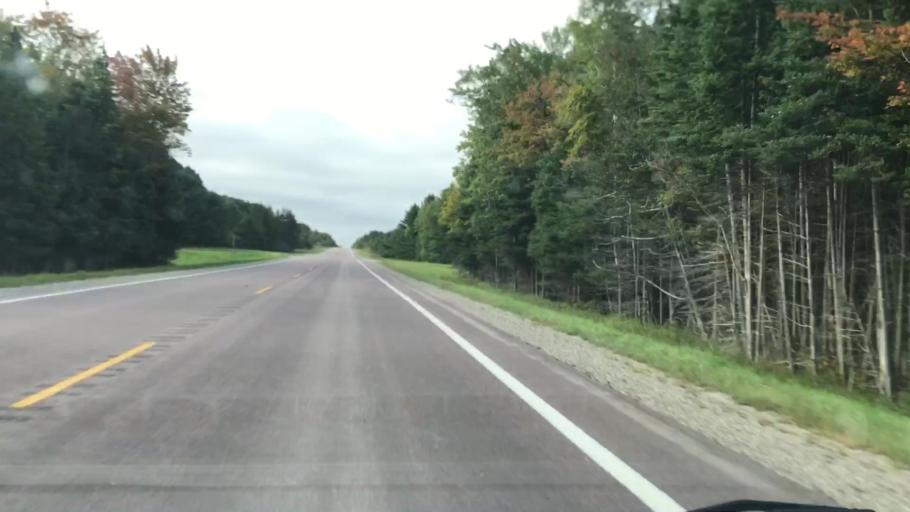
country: US
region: Michigan
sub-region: Luce County
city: Newberry
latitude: 46.2902
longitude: -85.5699
